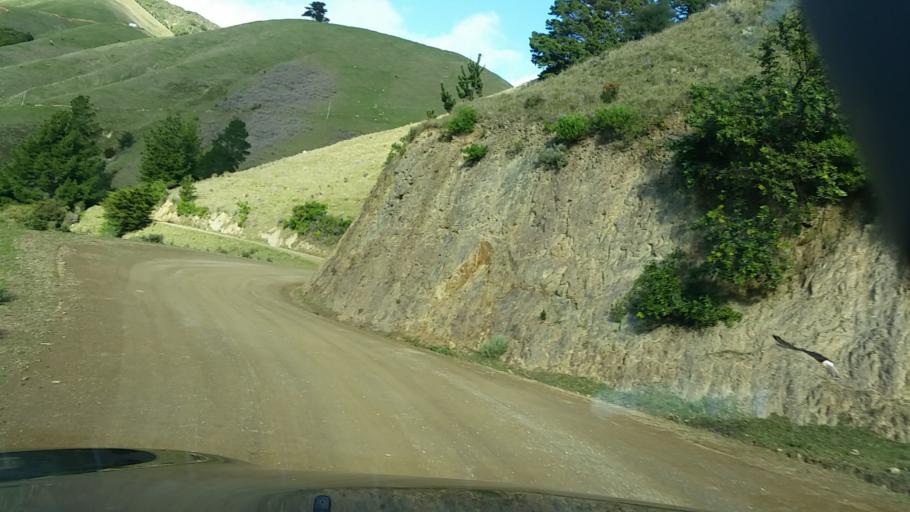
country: NZ
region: Marlborough
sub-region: Marlborough District
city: Picton
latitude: -40.9872
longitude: 173.8423
